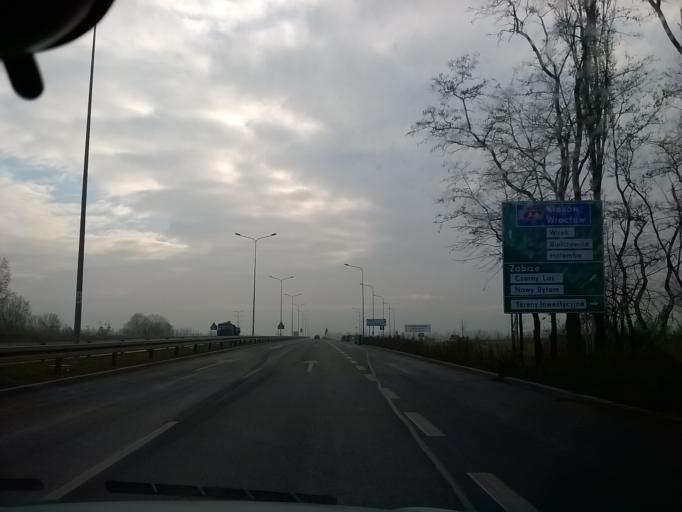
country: PL
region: Silesian Voivodeship
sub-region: Ruda Slaska
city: Ruda Slaska
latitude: 50.2871
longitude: 18.8499
